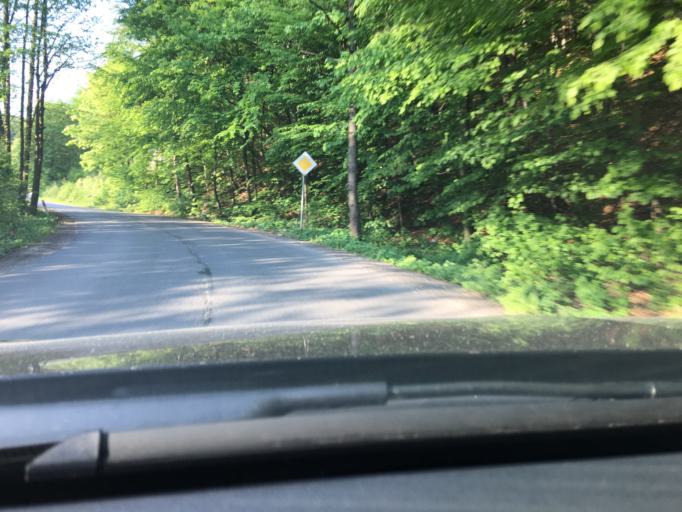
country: PL
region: Lesser Poland Voivodeship
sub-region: Powiat krakowski
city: Jerzmanowice
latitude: 50.1948
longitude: 19.7265
